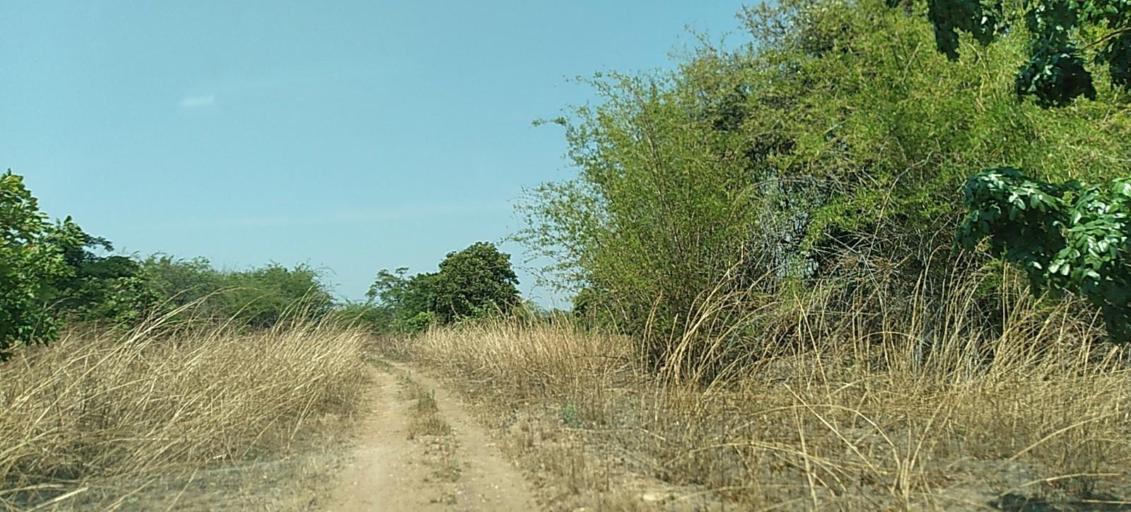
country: ZM
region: Copperbelt
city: Luanshya
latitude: -12.9856
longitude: 28.3270
